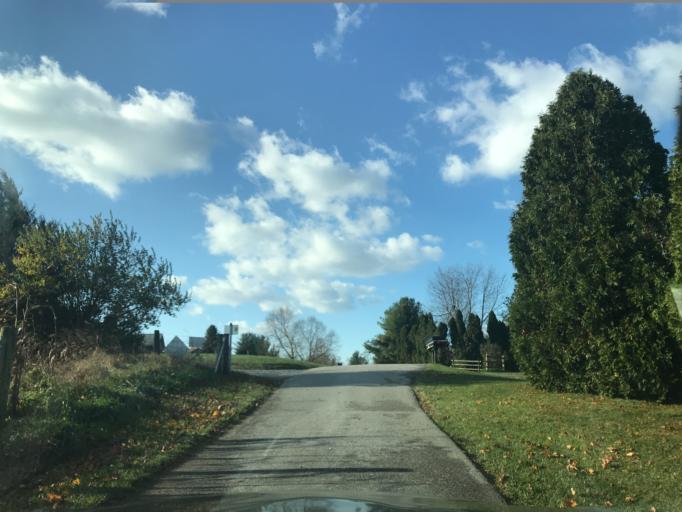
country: US
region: Maryland
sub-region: Carroll County
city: Taneytown
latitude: 39.6279
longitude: -77.0968
